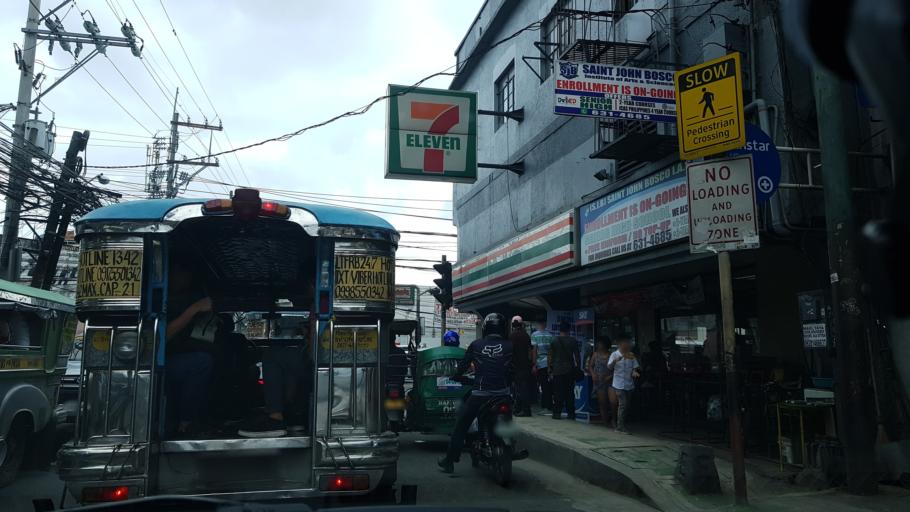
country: PH
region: Metro Manila
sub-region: Pasig
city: Pasig City
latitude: 14.5664
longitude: 121.0761
